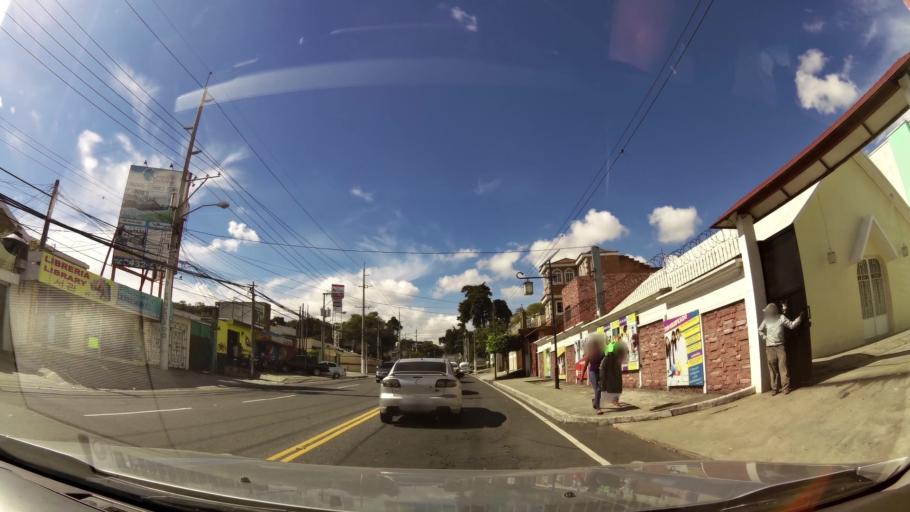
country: GT
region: Guatemala
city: Mixco
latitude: 14.6335
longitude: -90.5646
